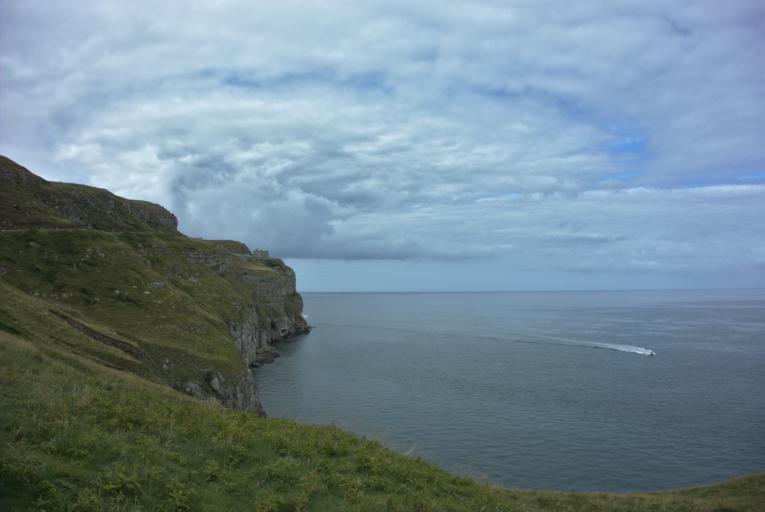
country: GB
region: Wales
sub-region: Conwy
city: Llandudno
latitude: 53.3406
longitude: -3.8556
